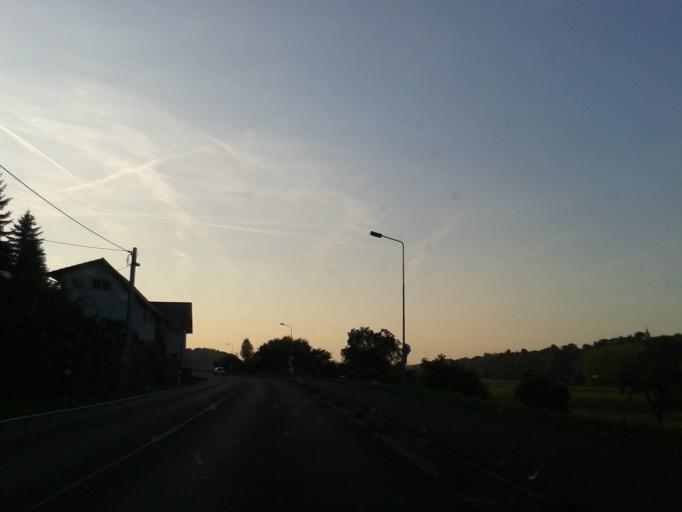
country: DE
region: Saxony
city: Meissen
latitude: 51.1871
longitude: 13.4365
